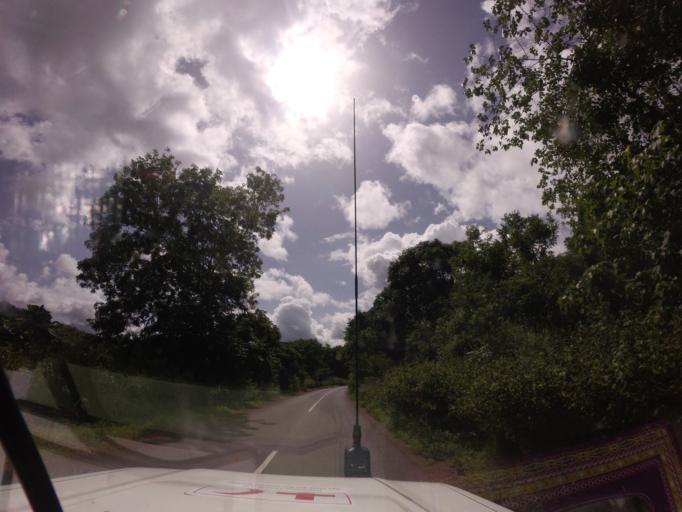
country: GN
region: Mamou
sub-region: Mamou Prefecture
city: Mamou
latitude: 10.3194
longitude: -12.0171
